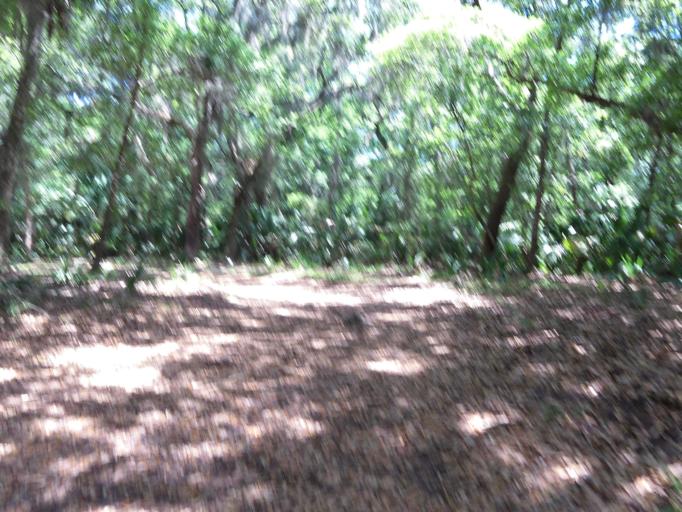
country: US
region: Florida
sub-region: Duval County
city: Atlantic Beach
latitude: 30.4434
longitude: -81.4651
